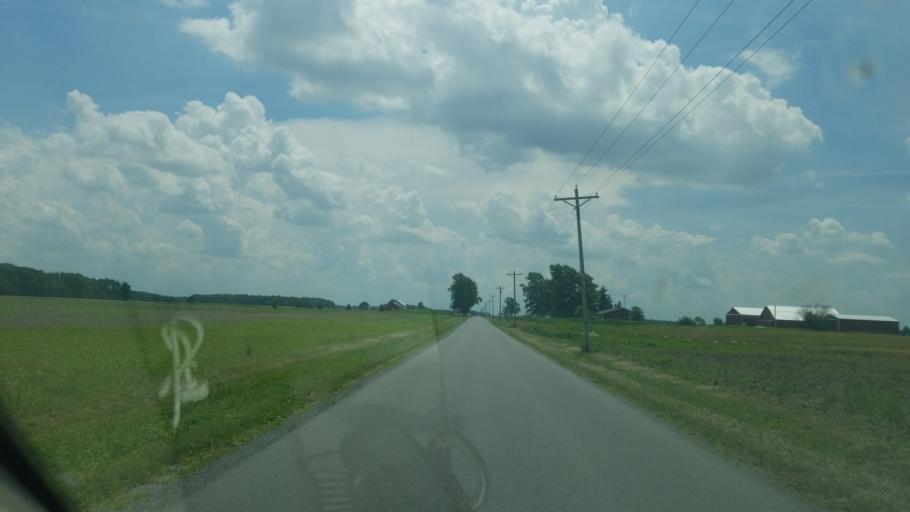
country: US
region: Ohio
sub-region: Hancock County
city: Arlington
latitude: 40.8435
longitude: -83.5999
